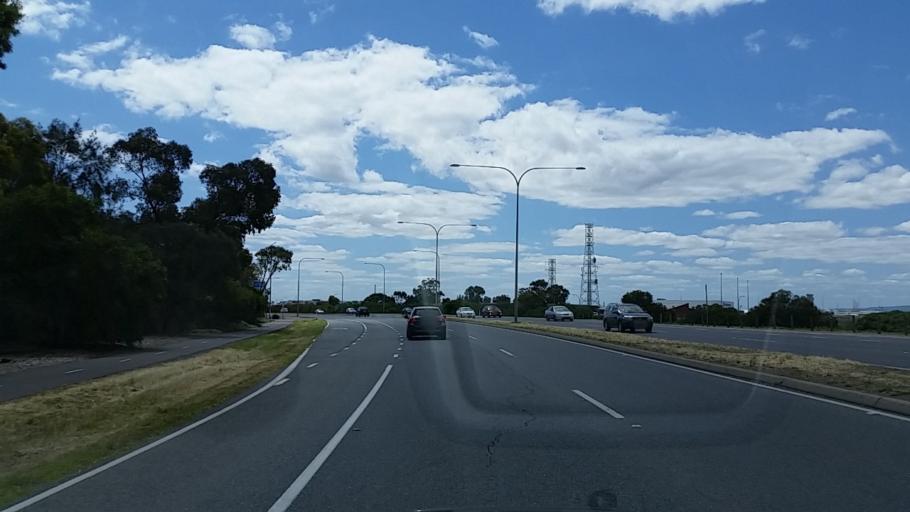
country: AU
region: South Australia
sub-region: Holdfast Bay
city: Glenelg East
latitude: -34.9536
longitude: 138.5179
